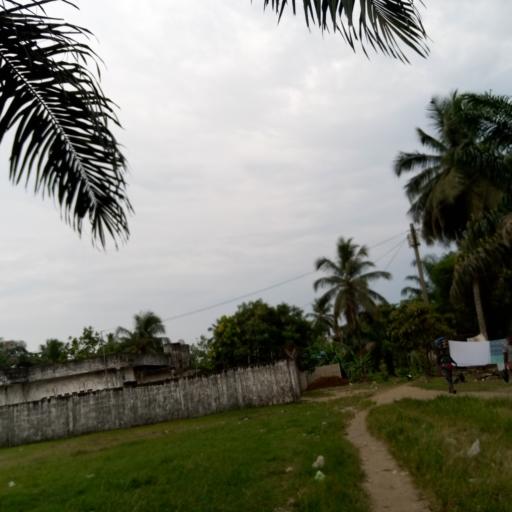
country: LR
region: Montserrado
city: Monrovia
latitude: 6.2901
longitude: -10.6815
